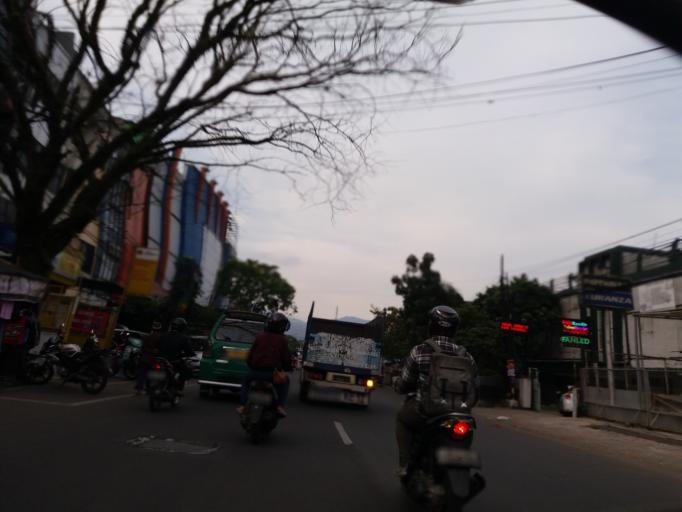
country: ID
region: West Java
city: Bandung
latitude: -6.9045
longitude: 107.6512
